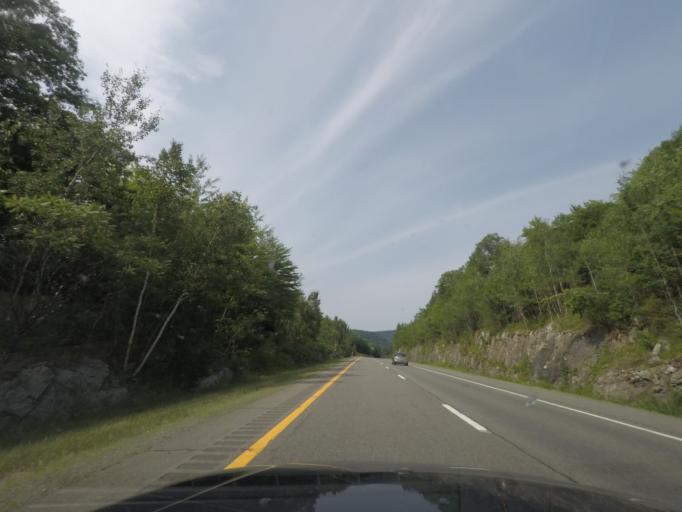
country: US
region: New York
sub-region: Essex County
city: Keeseville
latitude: 44.3645
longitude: -73.5295
